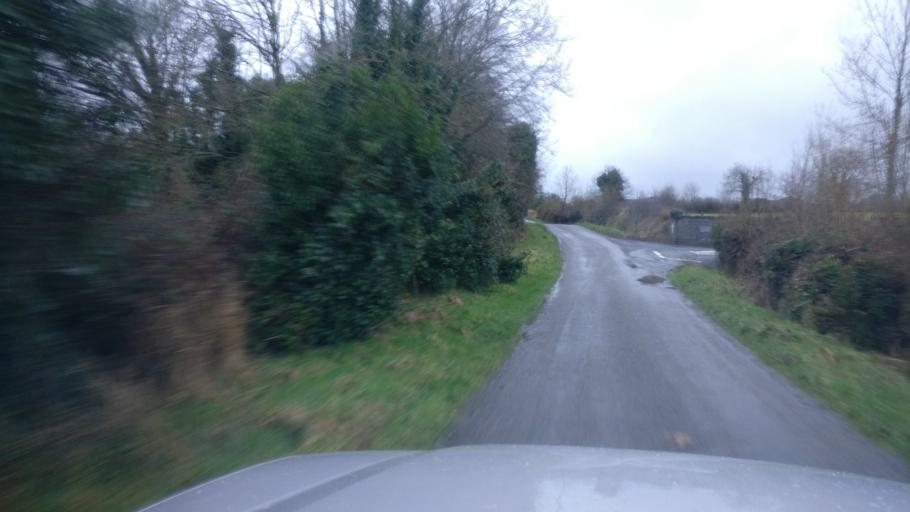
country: IE
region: Connaught
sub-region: County Galway
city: Ballinasloe
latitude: 53.2634
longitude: -8.3655
